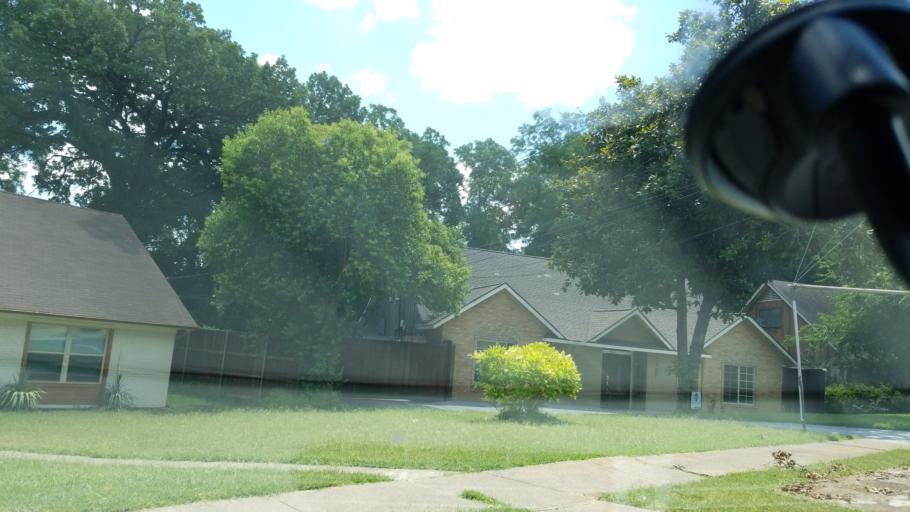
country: US
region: Texas
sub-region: Dallas County
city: Cockrell Hill
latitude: 32.6932
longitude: -96.8473
